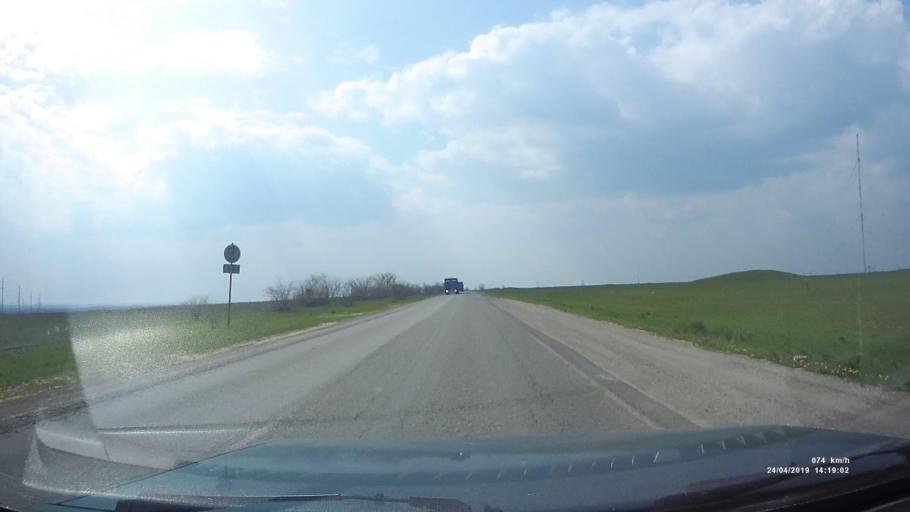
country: RU
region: Kalmykiya
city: Arshan'
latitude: 46.3043
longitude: 44.1827
